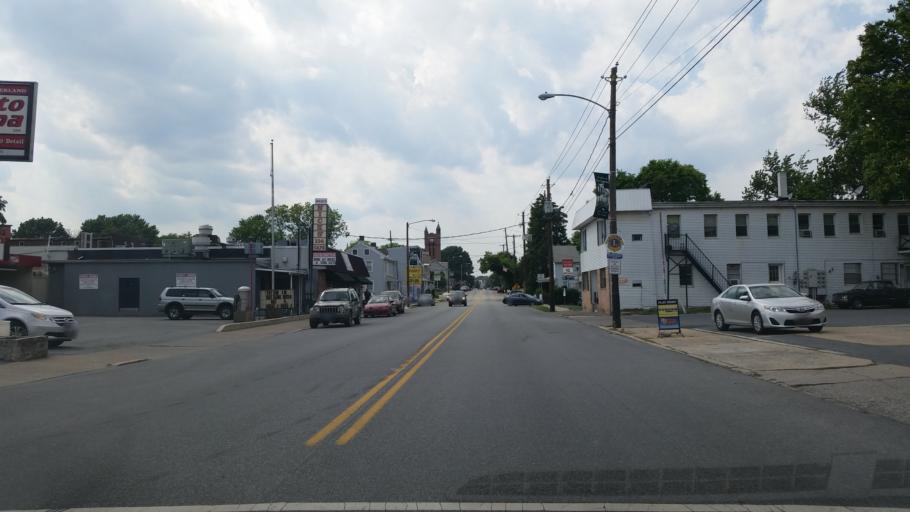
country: US
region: Pennsylvania
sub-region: Dauphin County
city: Steelton
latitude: 40.2246
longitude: -76.8612
